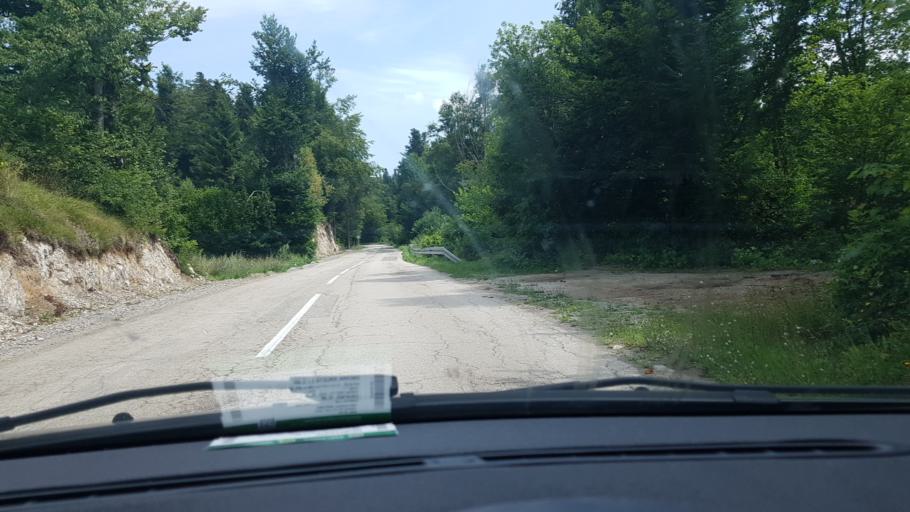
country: HR
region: Primorsko-Goranska
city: Hreljin
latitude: 45.3319
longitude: 14.6900
